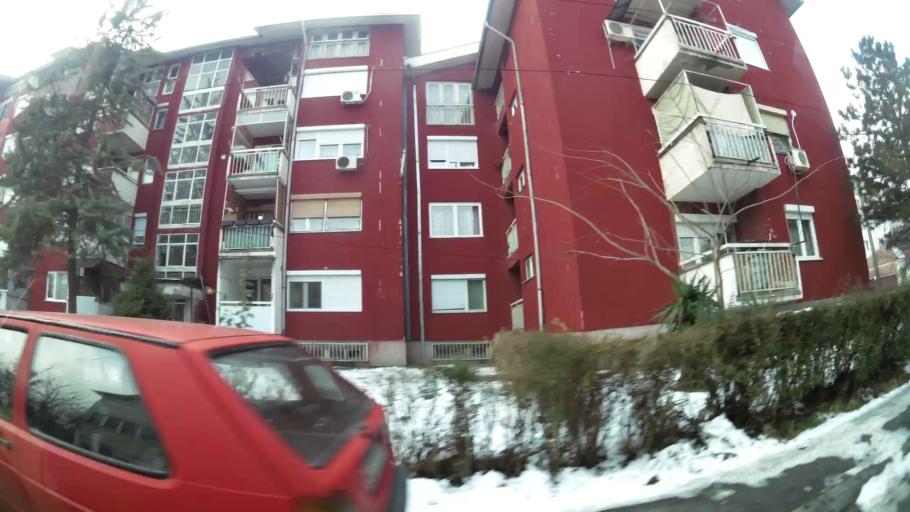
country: MK
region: Kisela Voda
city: Kisela Voda
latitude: 41.9937
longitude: 21.5071
